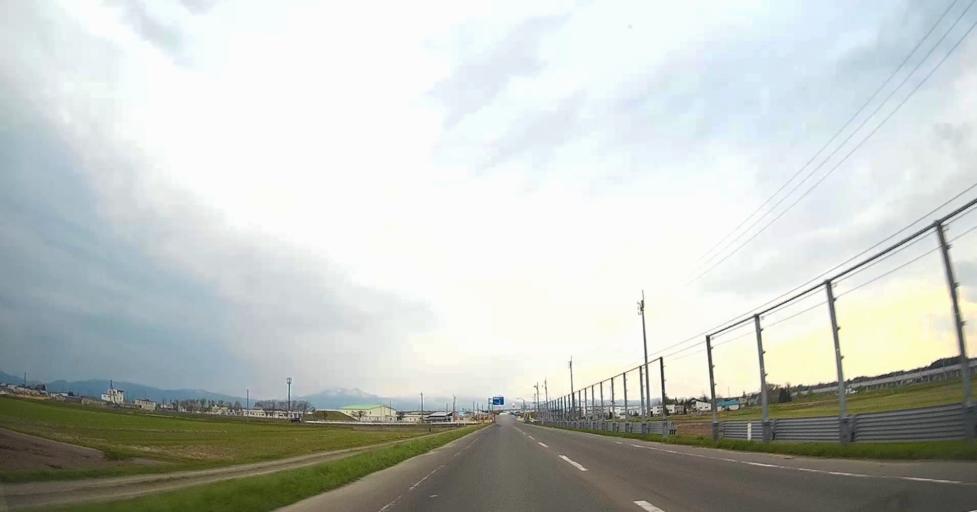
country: JP
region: Aomori
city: Aomori Shi
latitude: 40.8640
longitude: 140.6802
